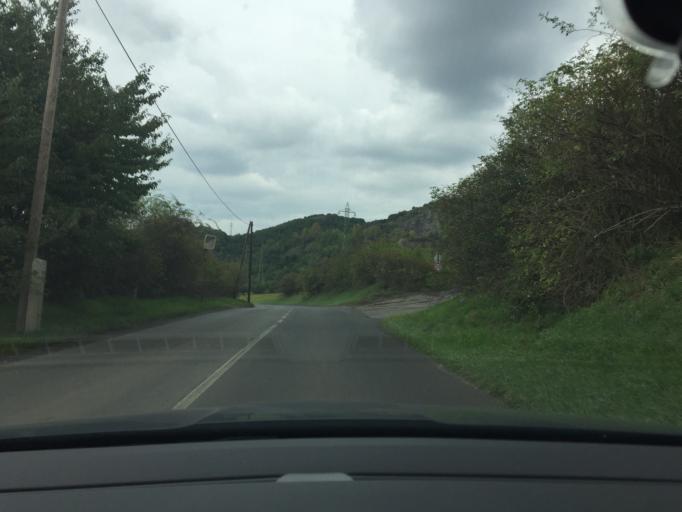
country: CZ
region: Ustecky
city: Lovosice
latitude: 50.5761
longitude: 14.0449
